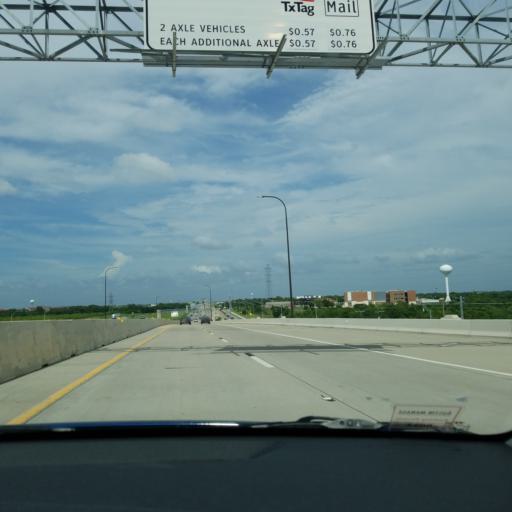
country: US
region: Texas
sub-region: Travis County
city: Manor
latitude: 30.3439
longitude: -97.5816
